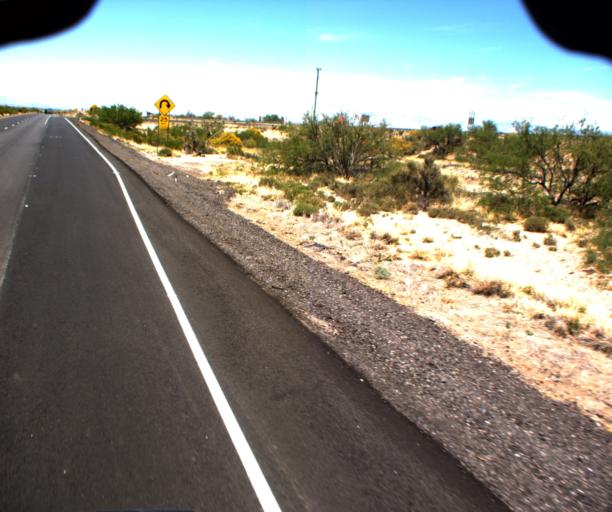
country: US
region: Arizona
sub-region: Pima County
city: Vail
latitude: 32.0076
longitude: -110.6908
